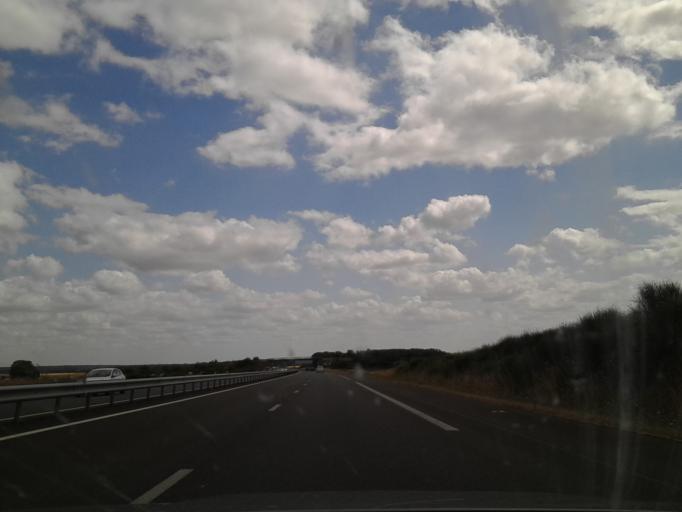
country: FR
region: Centre
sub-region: Departement du Cher
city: Levet
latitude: 46.8288
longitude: 2.4125
